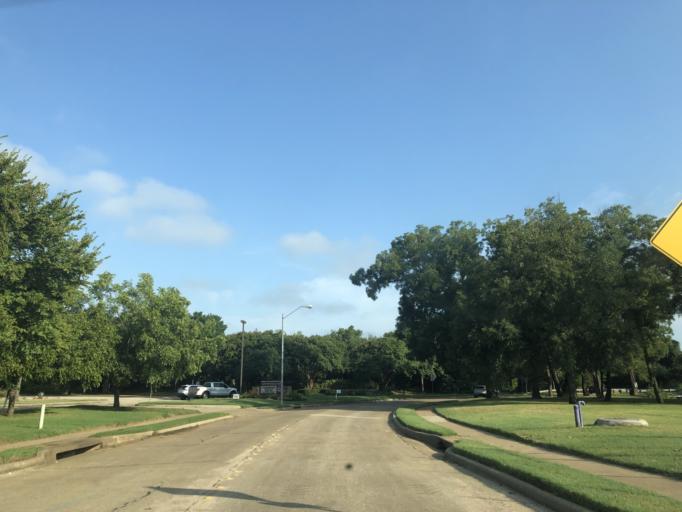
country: US
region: Texas
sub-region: Tarrant County
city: Euless
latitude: 32.8626
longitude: -97.0688
